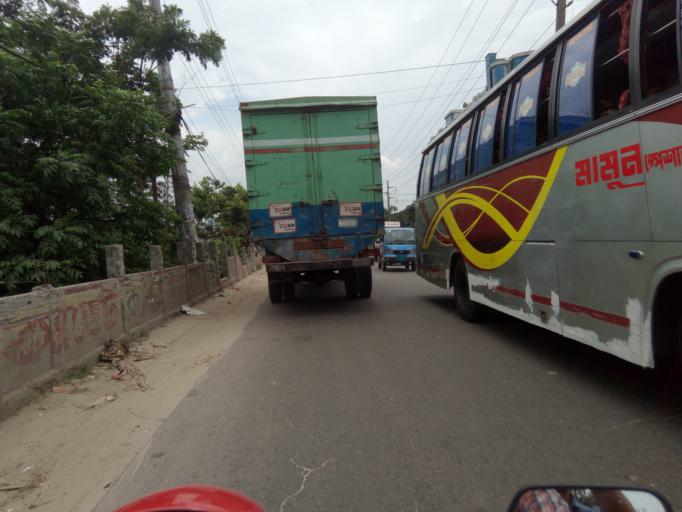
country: BD
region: Dhaka
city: Paltan
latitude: 23.7199
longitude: 90.4913
